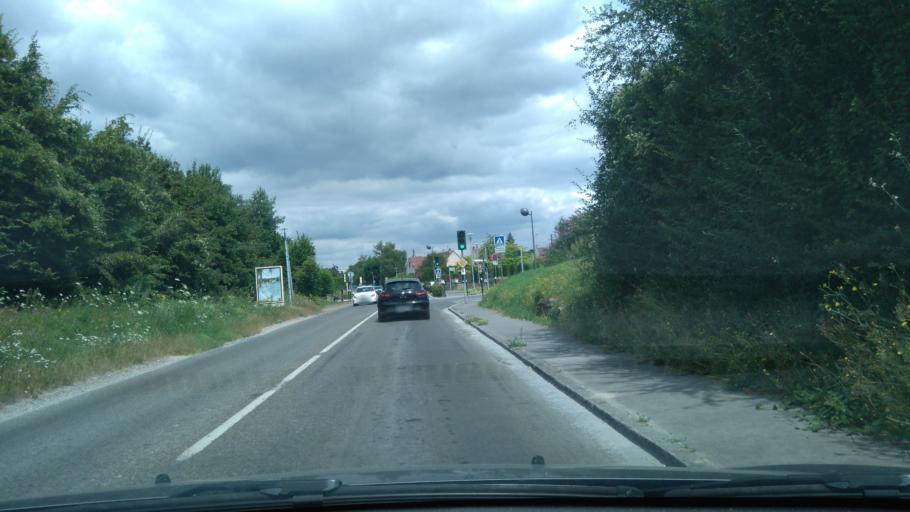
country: FR
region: Picardie
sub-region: Departement de l'Oise
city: Saint-Maximin
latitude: 49.2200
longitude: 2.4538
